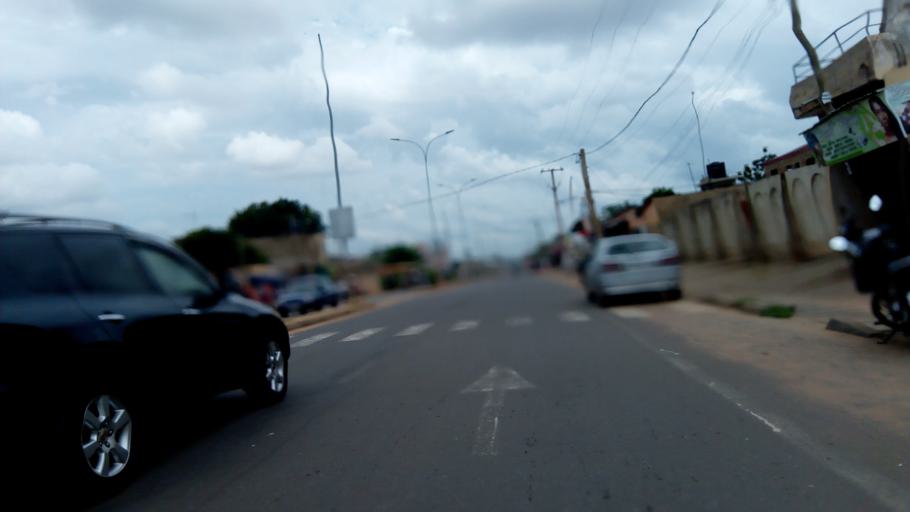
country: TG
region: Maritime
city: Lome
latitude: 6.2083
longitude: 1.1810
